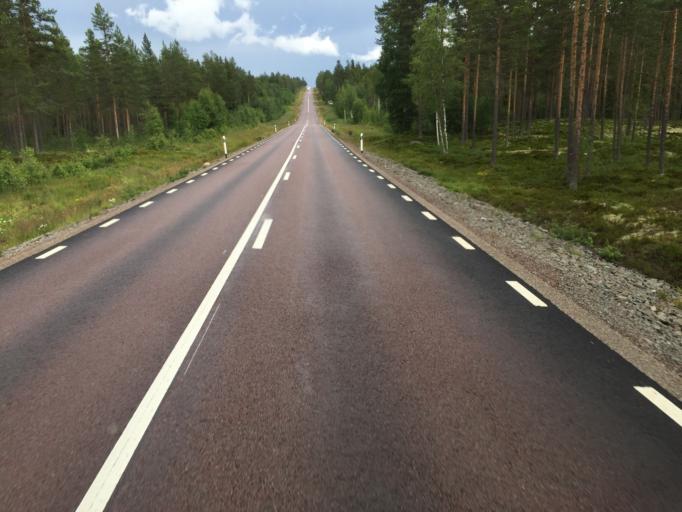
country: SE
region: Dalarna
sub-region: Malung-Saelens kommun
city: Malung
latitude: 60.8240
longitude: 13.9992
